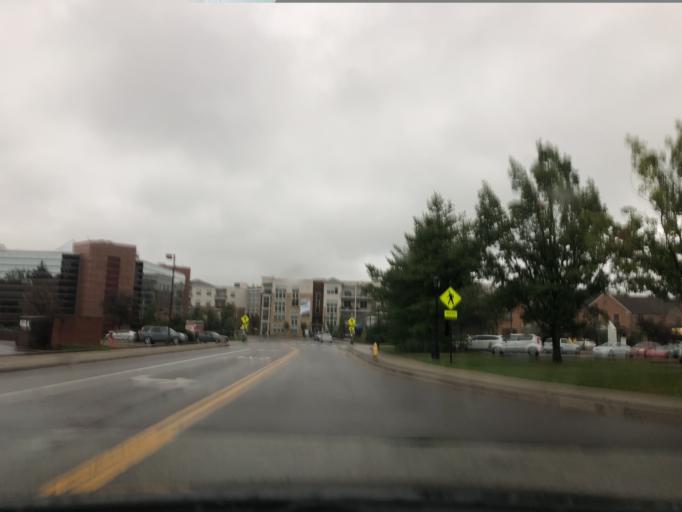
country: US
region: Ohio
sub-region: Hamilton County
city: Blue Ash
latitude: 39.2286
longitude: -84.3773
